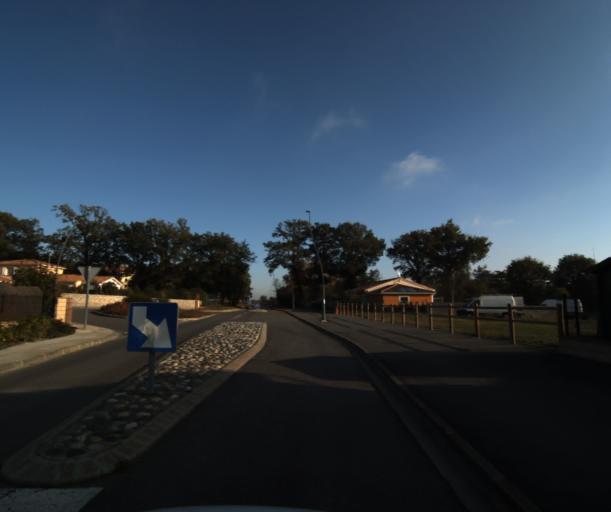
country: FR
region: Midi-Pyrenees
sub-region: Departement de la Haute-Garonne
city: Colomiers
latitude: 43.5947
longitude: 1.3432
